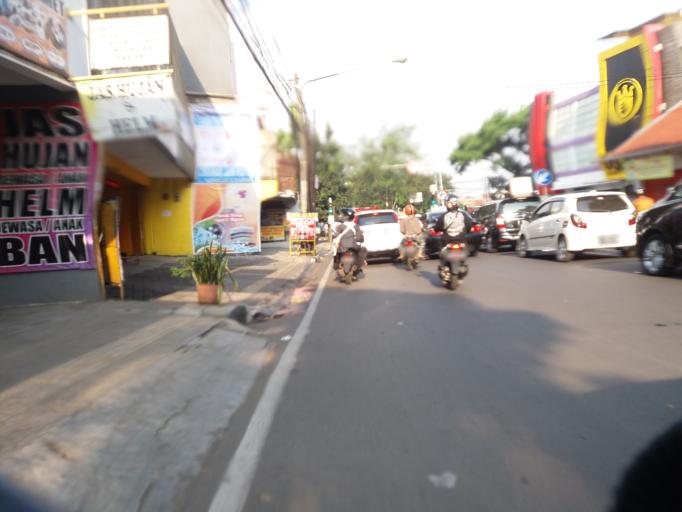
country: ID
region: West Java
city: Bandung
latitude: -6.9284
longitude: 107.6159
